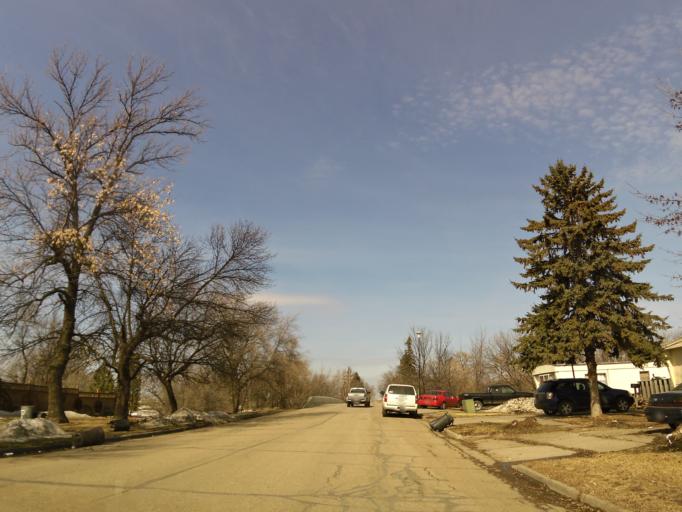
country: US
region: North Dakota
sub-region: Walsh County
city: Grafton
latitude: 48.4226
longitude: -97.4086
